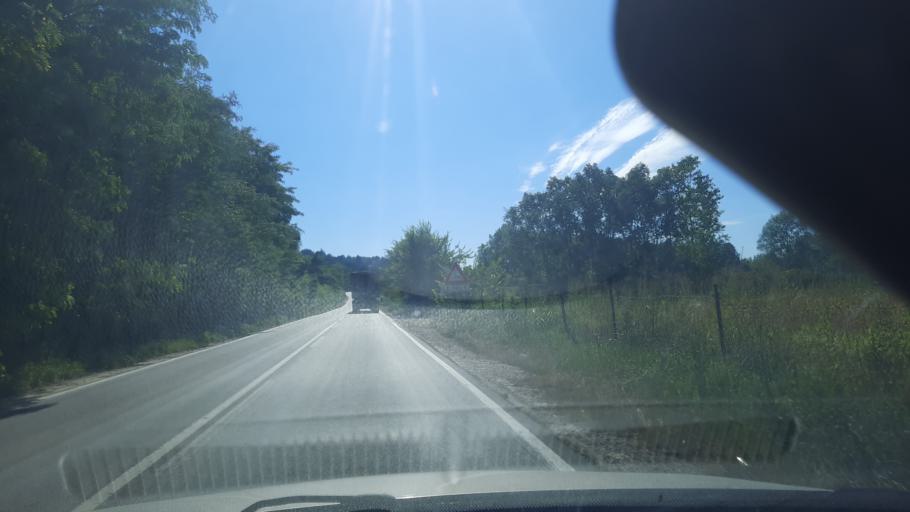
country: RS
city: Veternik
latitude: 45.2104
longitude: 19.7845
